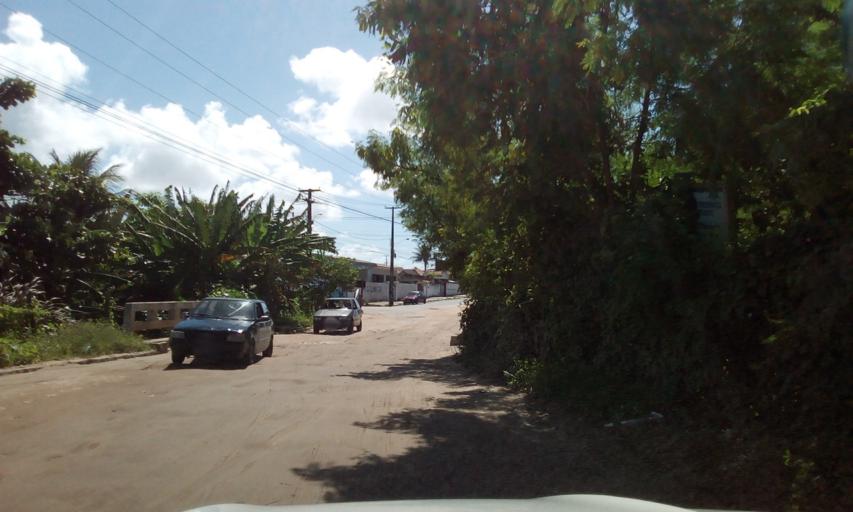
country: BR
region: Paraiba
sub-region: Joao Pessoa
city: Joao Pessoa
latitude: -7.1716
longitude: -34.8313
